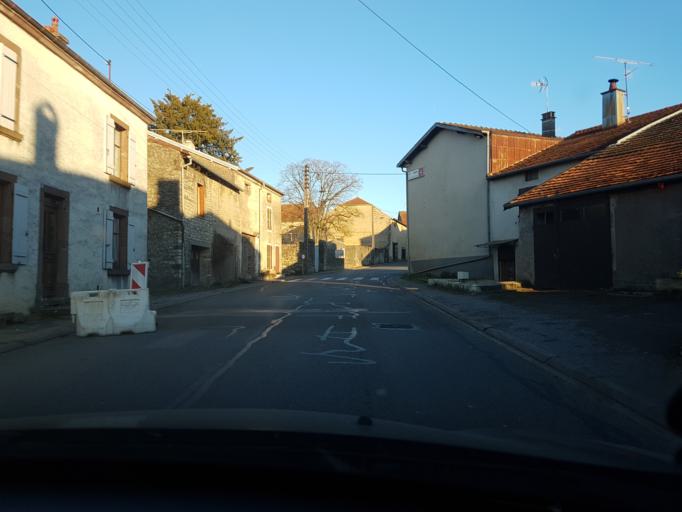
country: FR
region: Franche-Comte
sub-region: Departement de la Haute-Saone
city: Faverney
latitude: 47.9234
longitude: 6.0963
